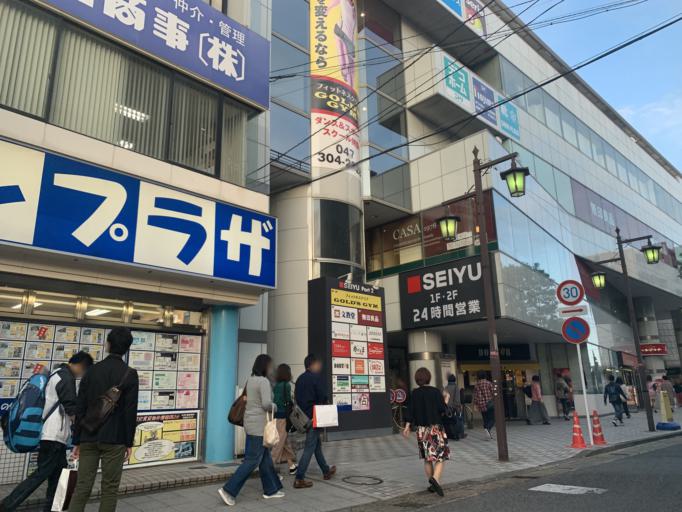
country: JP
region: Tokyo
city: Urayasu
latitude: 35.6658
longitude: 139.8934
